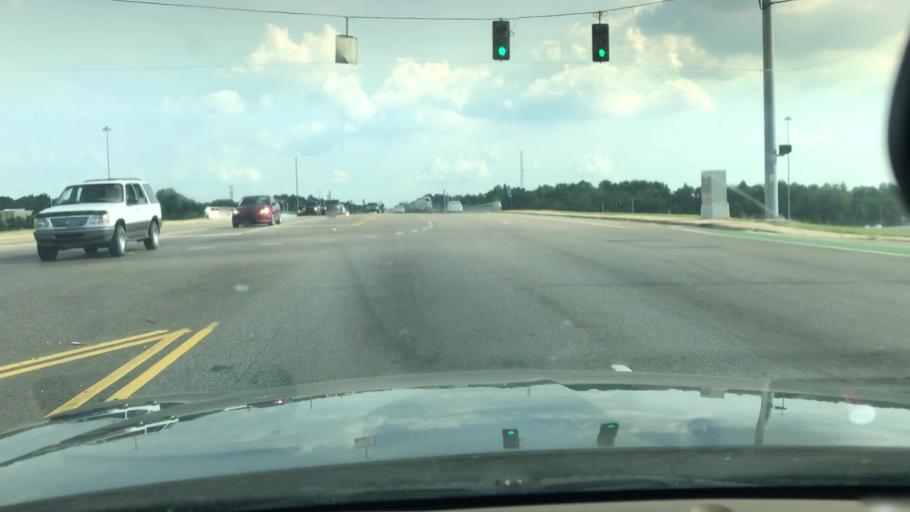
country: US
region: Tennessee
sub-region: Shelby County
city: Bartlett
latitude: 35.1766
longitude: -89.8364
